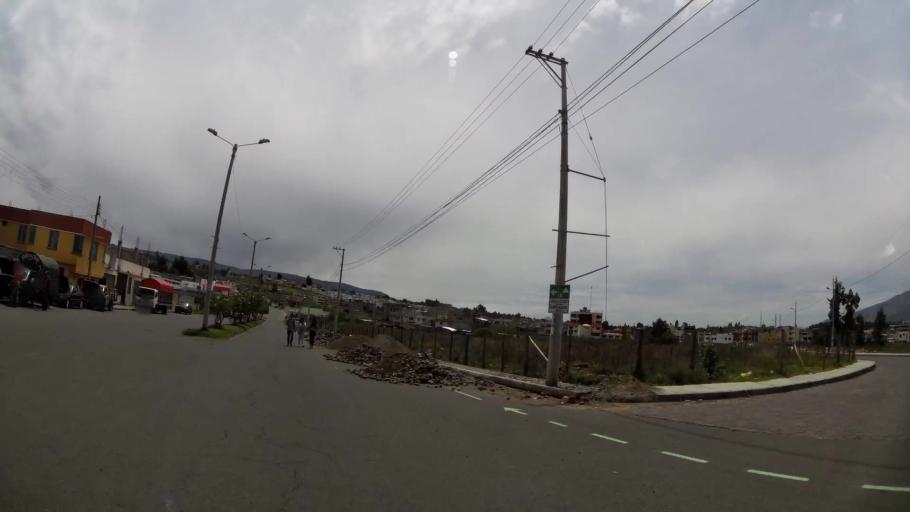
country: EC
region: Cotopaxi
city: San Miguel de Salcedo
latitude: -1.0392
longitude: -78.5866
